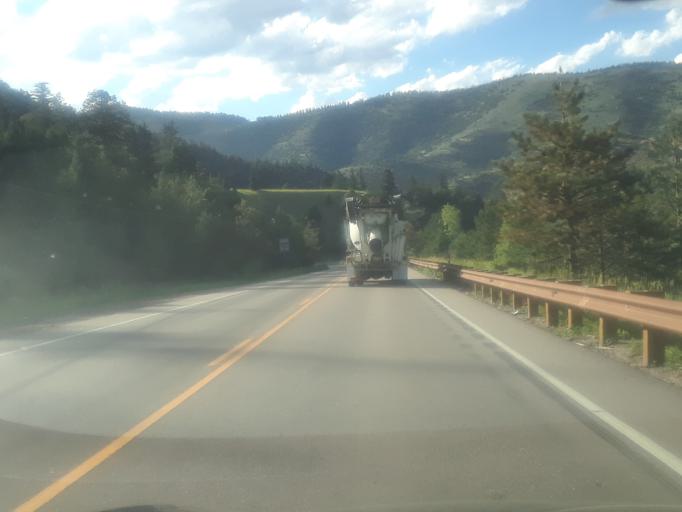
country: US
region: Colorado
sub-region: Clear Creek County
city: Idaho Springs
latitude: 39.7369
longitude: -105.4293
